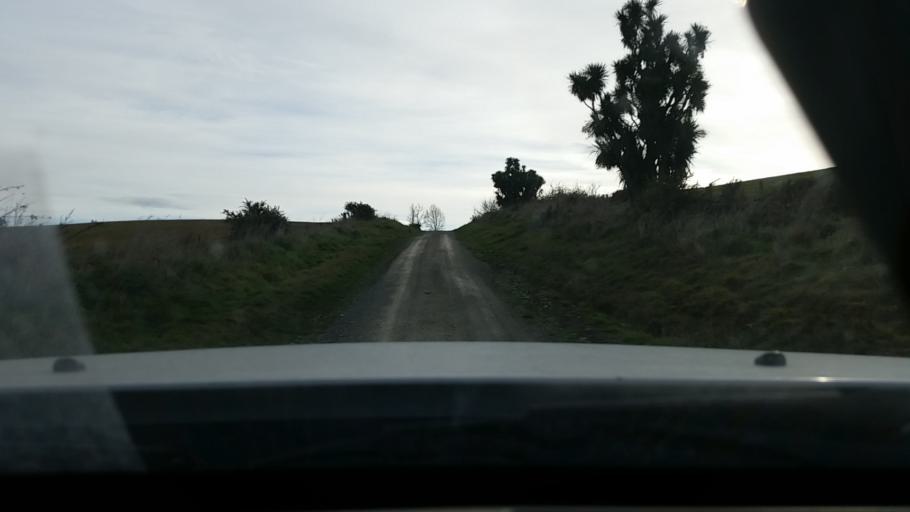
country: NZ
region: Canterbury
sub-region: Timaru District
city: Pleasant Point
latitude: -44.2007
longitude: 171.1870
